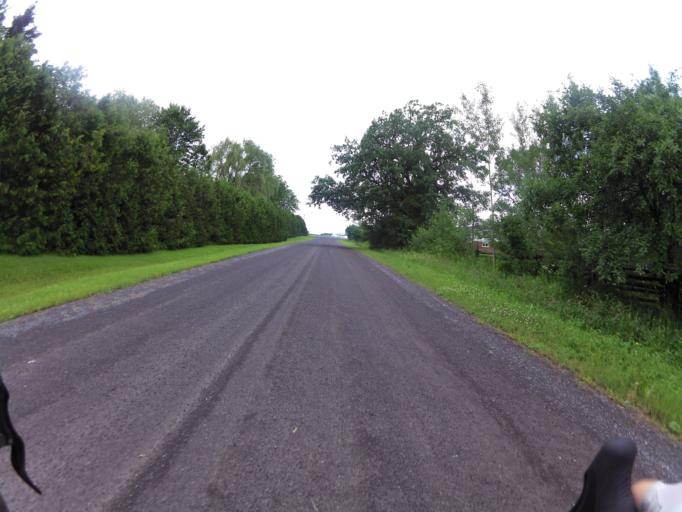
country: CA
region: Ontario
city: Bells Corners
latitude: 45.2543
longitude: -75.8735
